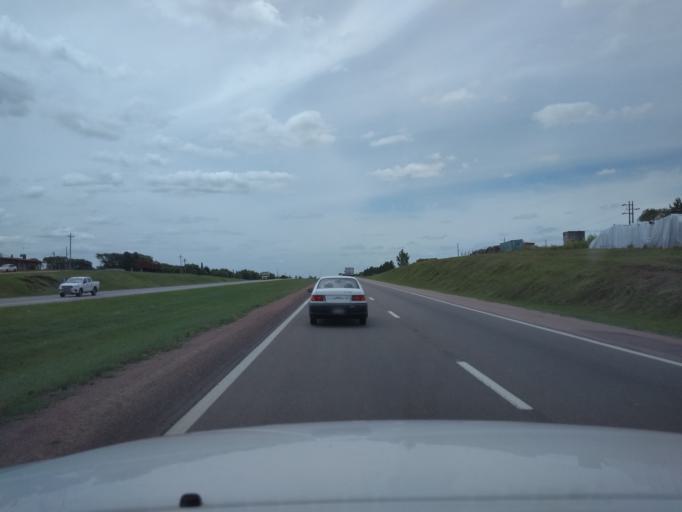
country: UY
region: Canelones
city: La Paz
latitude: -34.7437
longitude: -56.2521
